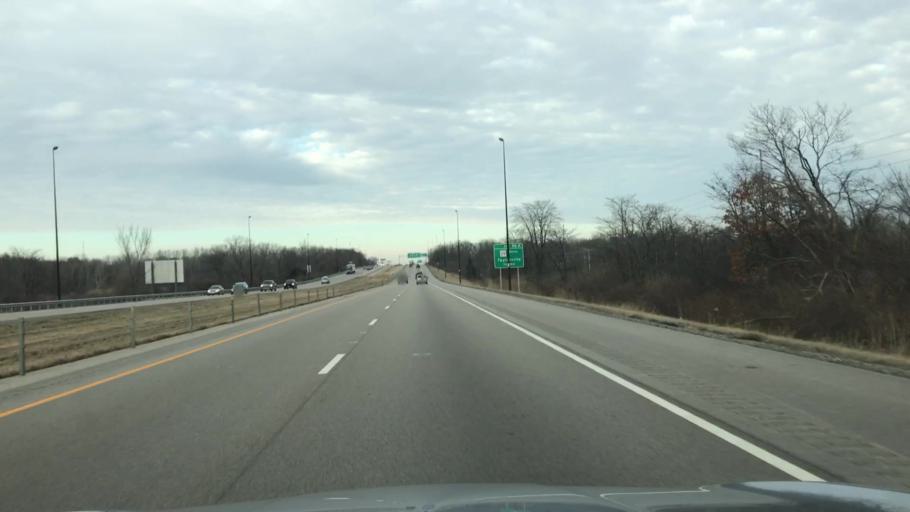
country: US
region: Illinois
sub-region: Sangamon County
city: Grandview
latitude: 39.7766
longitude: -89.6018
